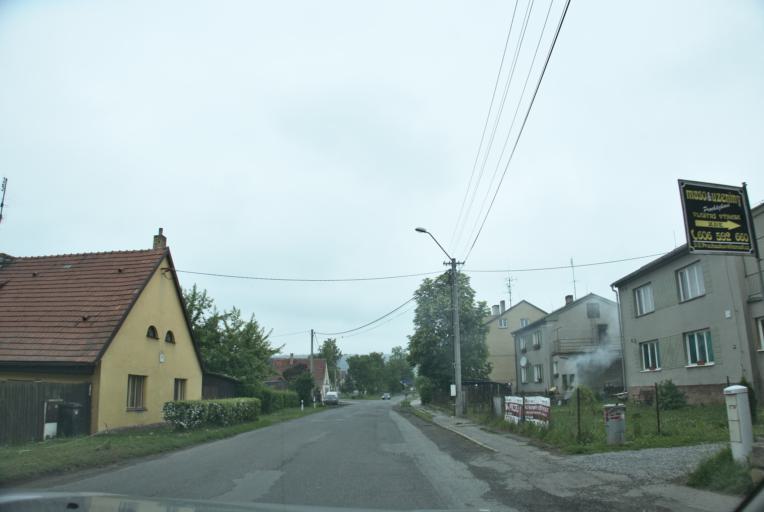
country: CZ
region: Plzensky
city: Zihle
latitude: 50.0425
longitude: 13.3806
